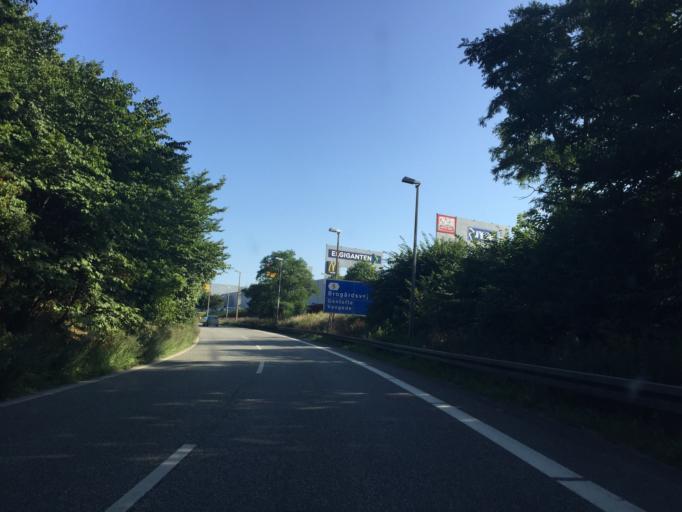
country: DK
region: Capital Region
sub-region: Lyngby-Tarbaek Kommune
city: Kongens Lyngby
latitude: 55.7561
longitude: 12.5192
